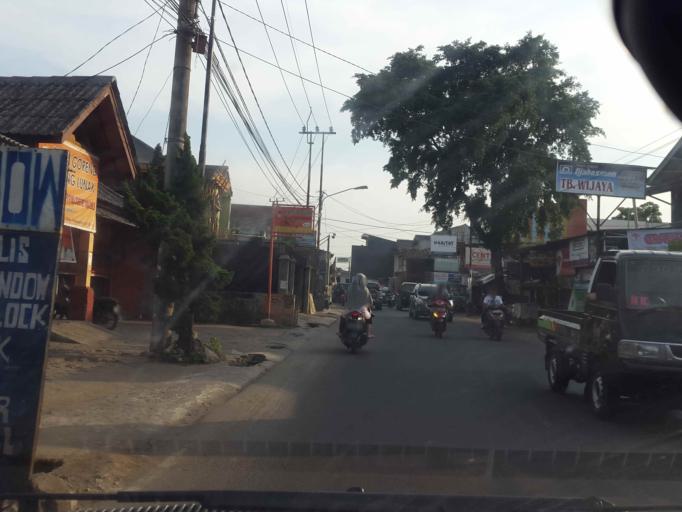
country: ID
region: West Java
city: Ciputat
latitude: -6.2466
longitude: 106.7009
